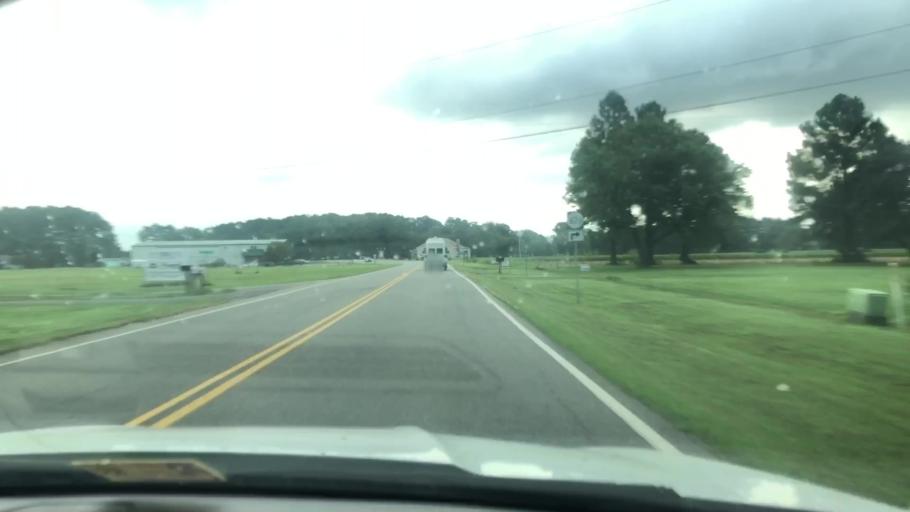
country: US
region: Virginia
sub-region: Middlesex County
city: Deltaville
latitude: 37.5983
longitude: -76.4483
